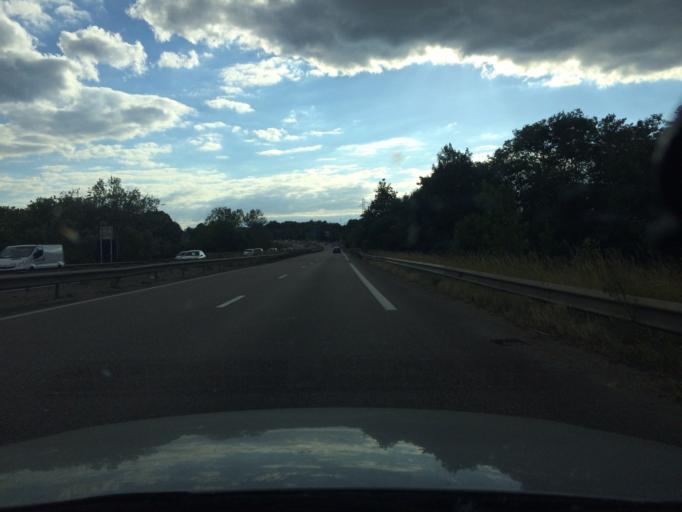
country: FR
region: Lorraine
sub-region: Departement de Meurthe-et-Moselle
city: Dommartin-les-Toul
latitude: 48.6563
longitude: 5.8977
